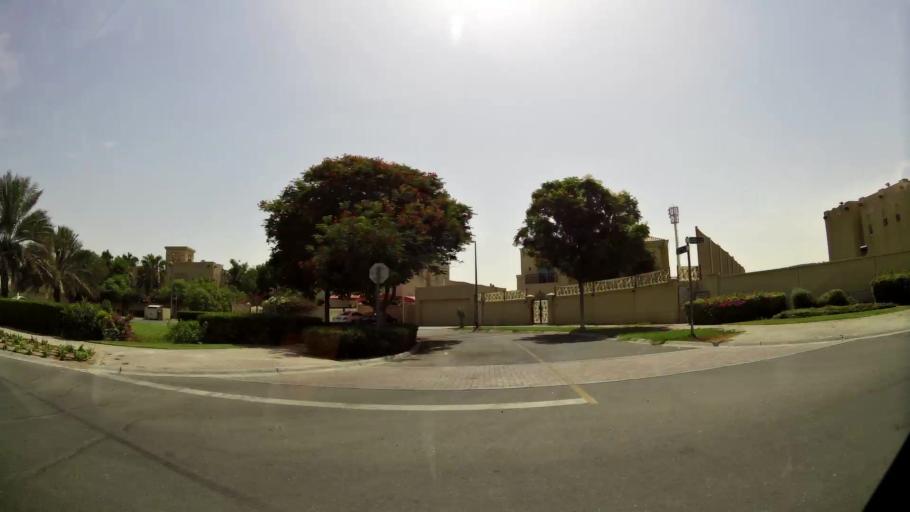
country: AE
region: Ash Shariqah
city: Sharjah
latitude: 25.1880
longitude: 55.4453
